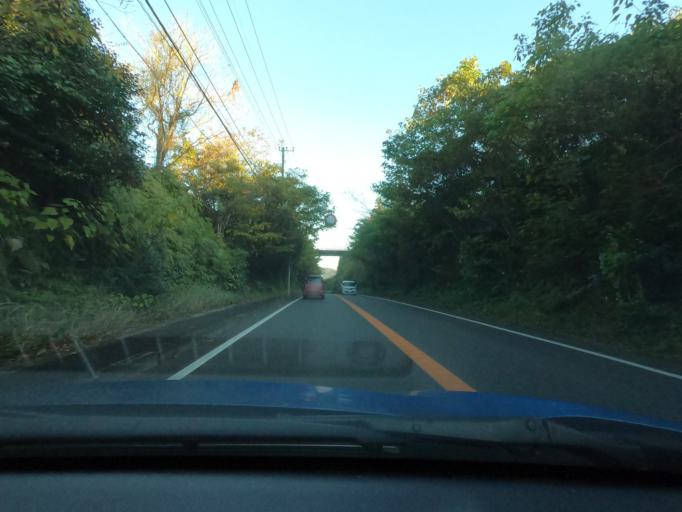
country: JP
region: Kagoshima
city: Satsumasendai
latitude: 31.8118
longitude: 130.3804
